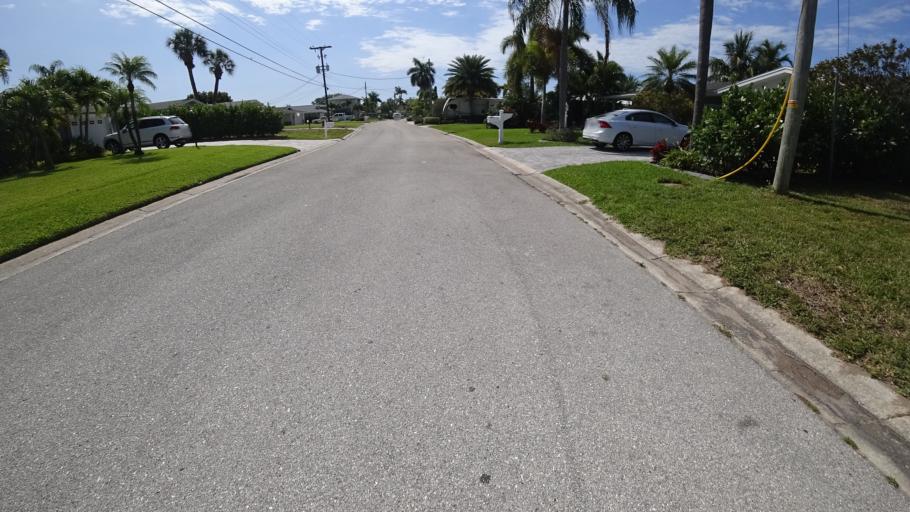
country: US
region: Florida
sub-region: Manatee County
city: Cortez
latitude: 27.4575
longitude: -82.6547
